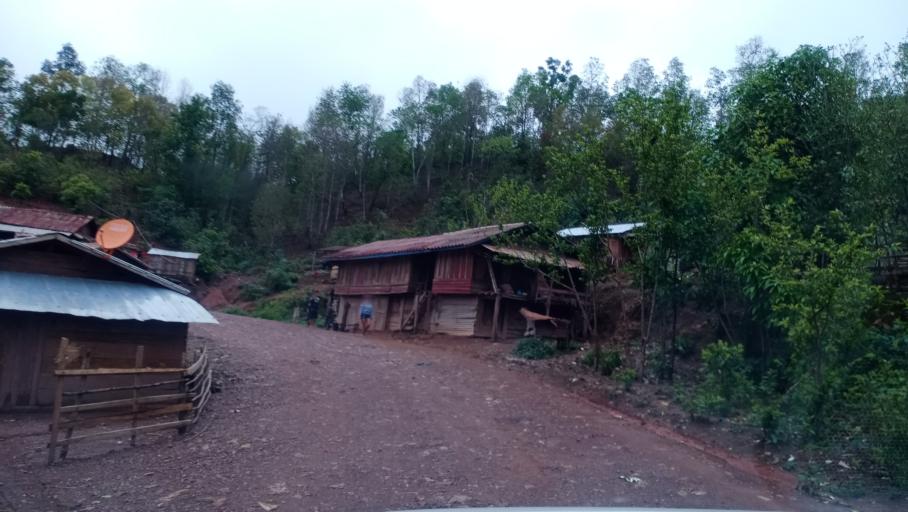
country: LA
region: Phongsali
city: Phongsali
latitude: 21.3380
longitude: 102.0825
